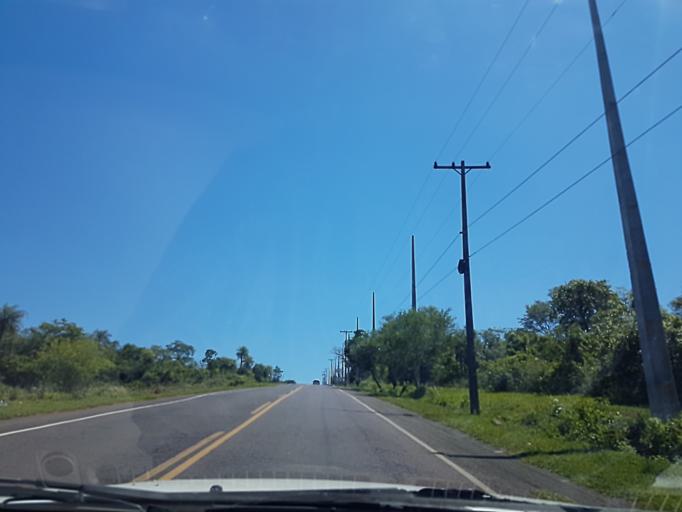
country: PY
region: Cordillera
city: Altos
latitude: -25.2526
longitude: -57.2407
